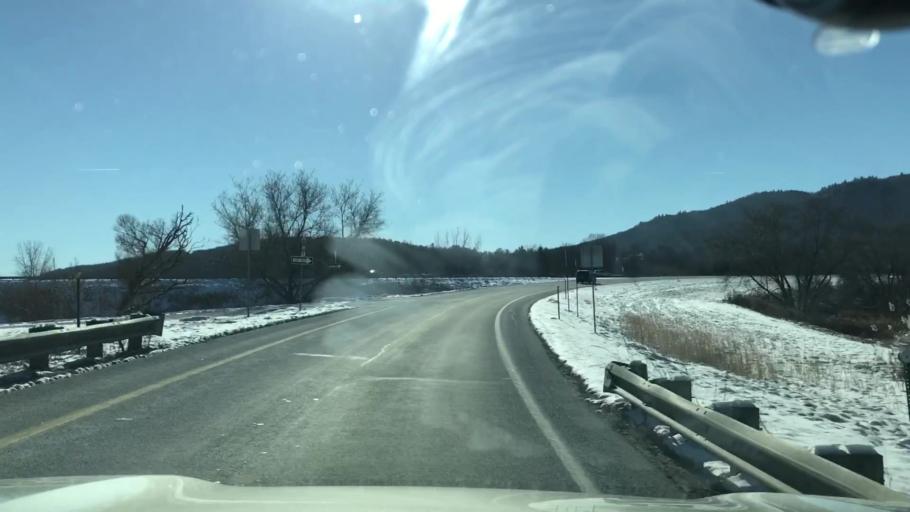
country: US
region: Vermont
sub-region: Rutland County
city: West Rutland
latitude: 43.5896
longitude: -73.0408
